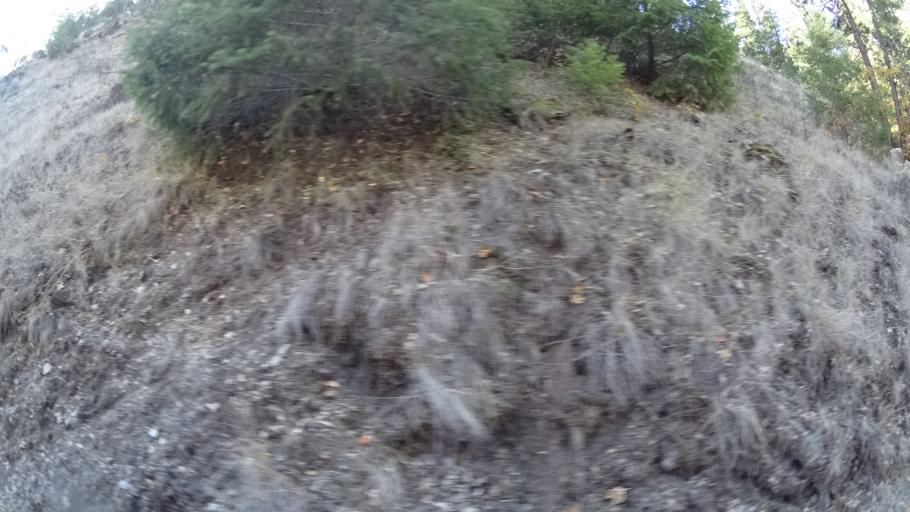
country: US
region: California
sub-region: Siskiyou County
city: Yreka
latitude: 41.8585
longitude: -122.7777
